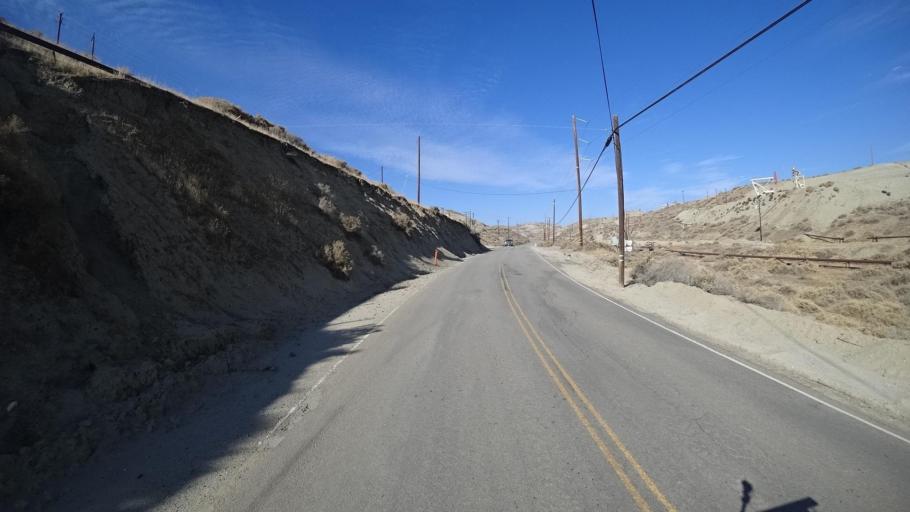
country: US
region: California
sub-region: Kern County
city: Oildale
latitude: 35.5690
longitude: -118.9580
